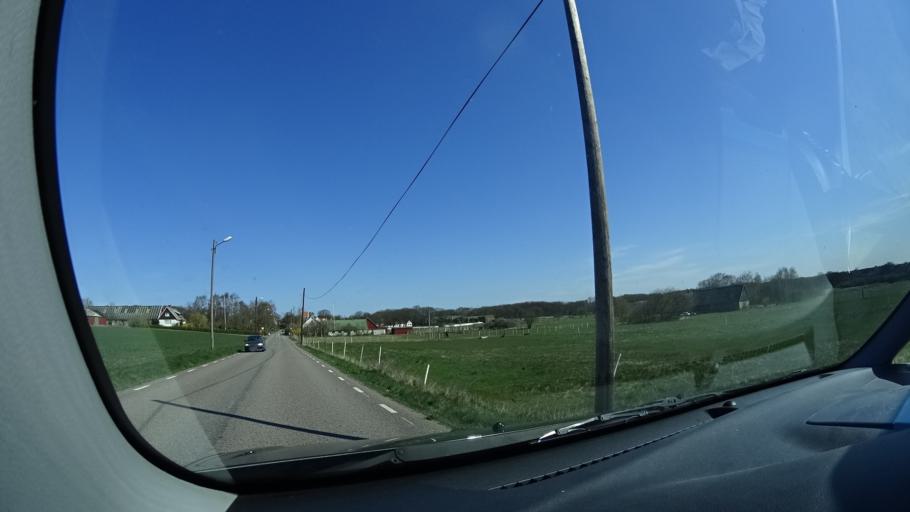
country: SE
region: Skane
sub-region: Hoganas Kommun
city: Hoganas
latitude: 56.2547
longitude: 12.5705
